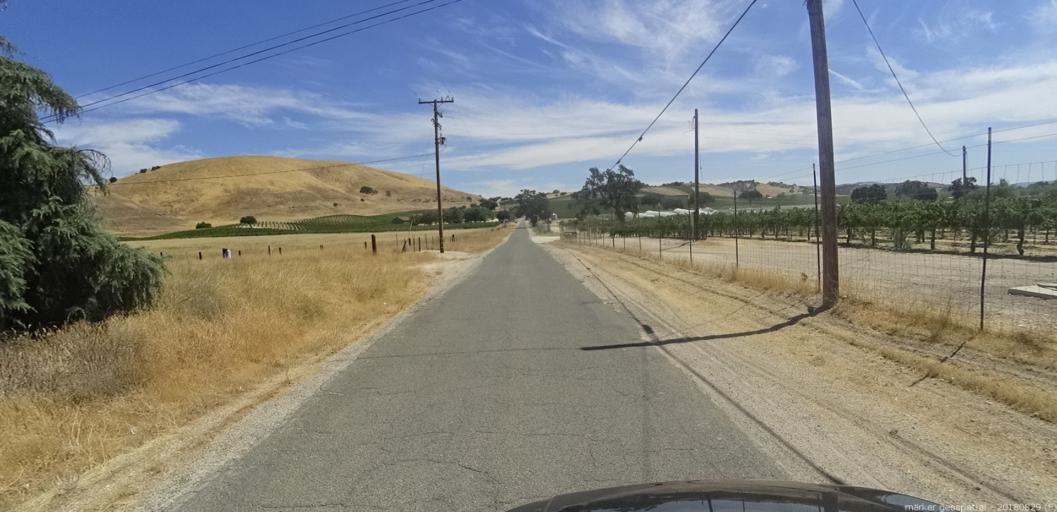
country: US
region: California
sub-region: San Luis Obispo County
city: Lake Nacimiento
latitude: 35.9081
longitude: -121.0244
